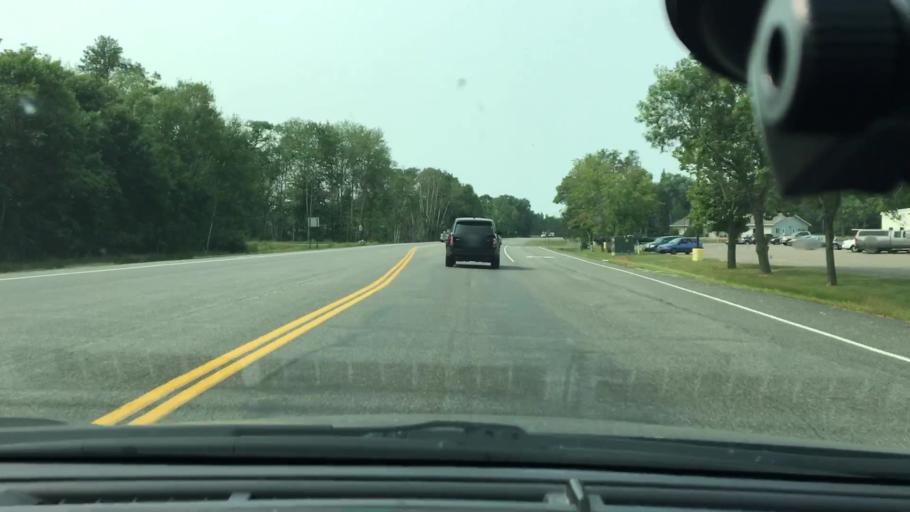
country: US
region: Minnesota
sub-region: Crow Wing County
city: Breezy Point
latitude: 46.4869
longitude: -94.1578
